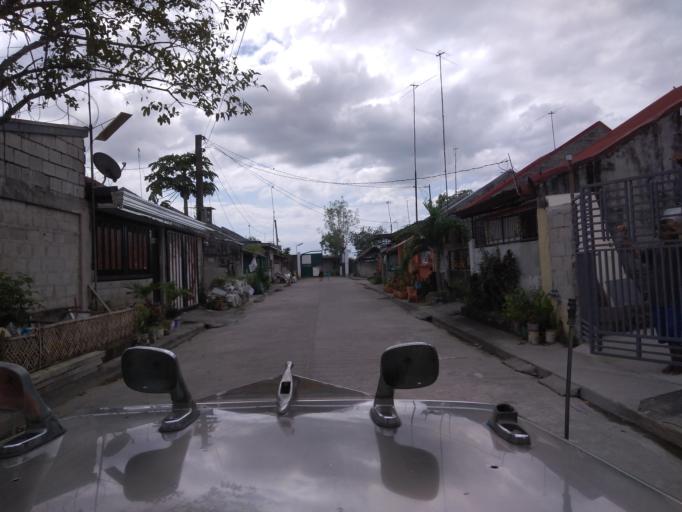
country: PH
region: Central Luzon
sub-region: Province of Pampanga
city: Pandacaqui
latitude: 15.1764
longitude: 120.6627
